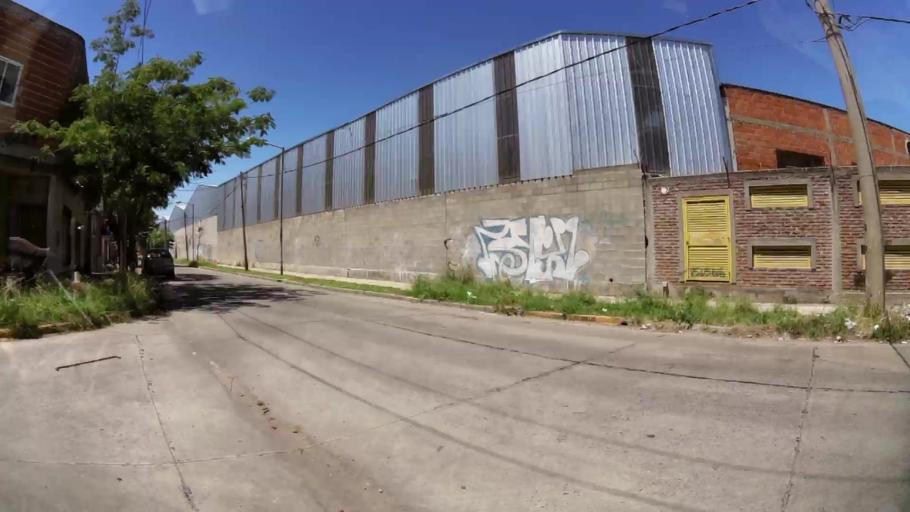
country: AR
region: Buenos Aires
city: Caseros
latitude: -34.5920
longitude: -58.5497
